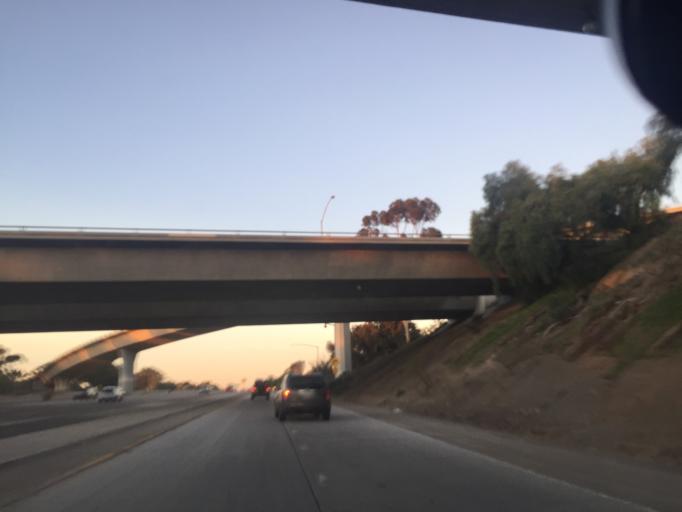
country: US
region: California
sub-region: San Diego County
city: Imperial Beach
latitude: 32.5680
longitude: -117.0403
